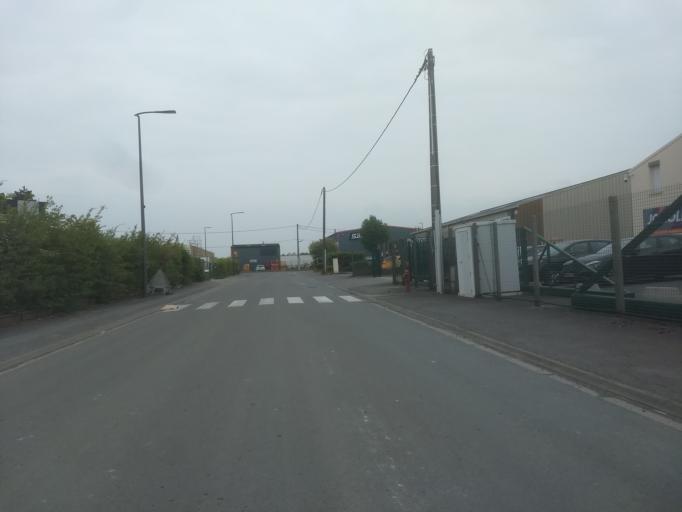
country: FR
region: Nord-Pas-de-Calais
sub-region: Departement du Pas-de-Calais
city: Saint-Laurent-Blangy
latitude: 50.2894
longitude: 2.8038
